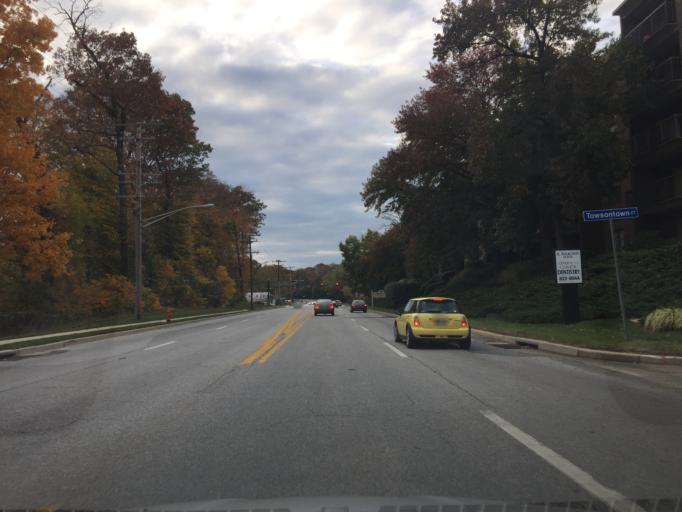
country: US
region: Maryland
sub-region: Baltimore County
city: Towson
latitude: 39.3958
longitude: -76.6173
